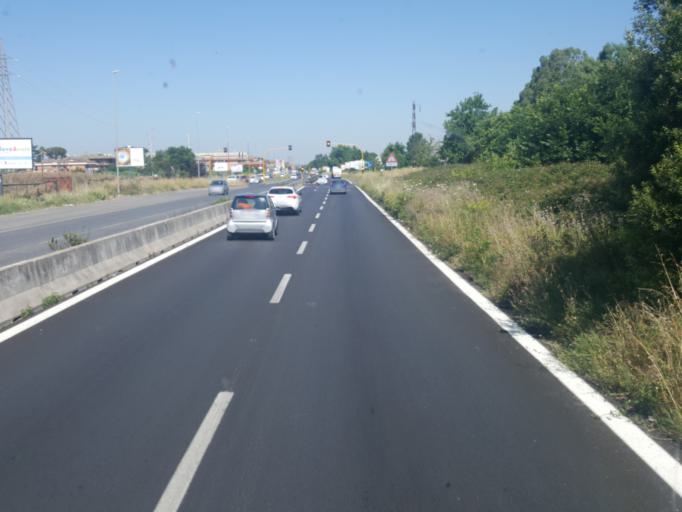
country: IT
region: Latium
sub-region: Citta metropolitana di Roma Capitale
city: Ciampino
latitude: 41.8338
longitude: 12.6078
